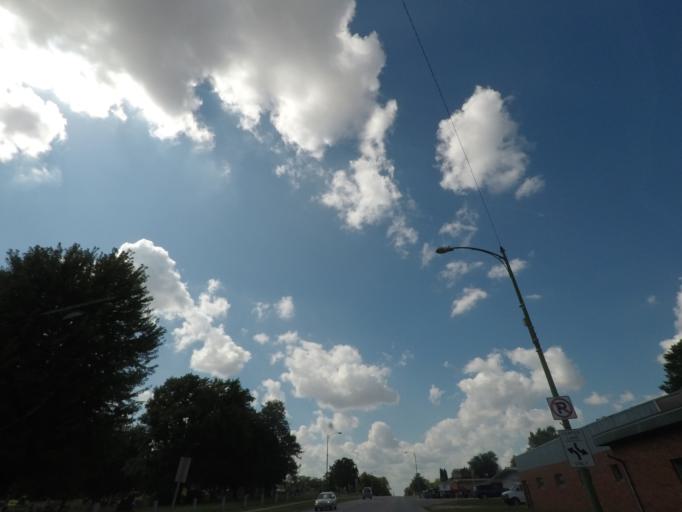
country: US
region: Iowa
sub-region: Story County
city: Nevada
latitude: 42.0228
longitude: -93.4608
